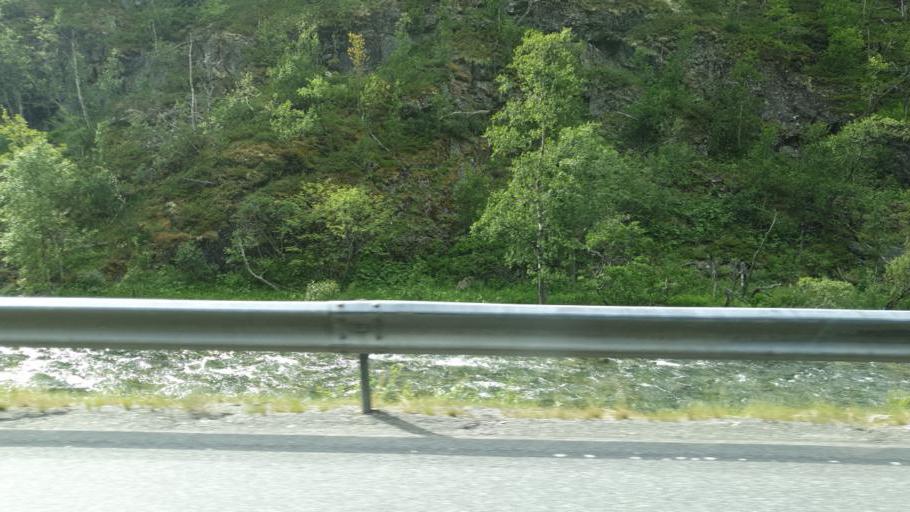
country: NO
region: Sor-Trondelag
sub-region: Oppdal
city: Oppdal
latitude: 62.3606
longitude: 9.6373
